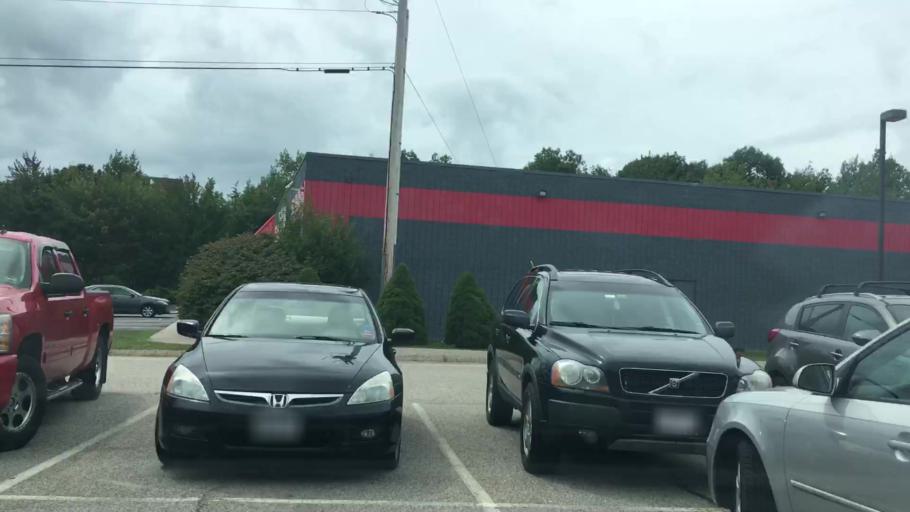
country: US
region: Maine
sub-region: Cumberland County
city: South Portland Gardens
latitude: 43.6287
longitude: -70.3455
